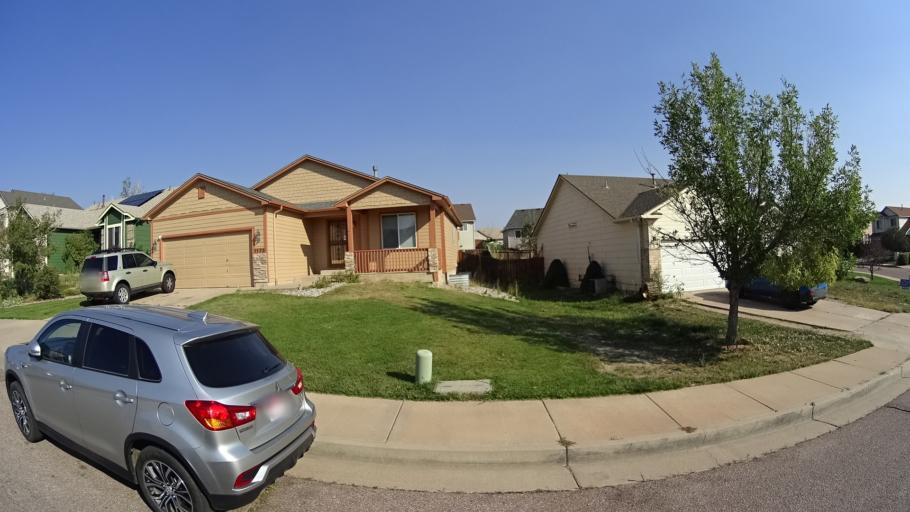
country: US
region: Colorado
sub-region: El Paso County
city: Stratmoor
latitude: 38.7699
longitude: -104.8082
